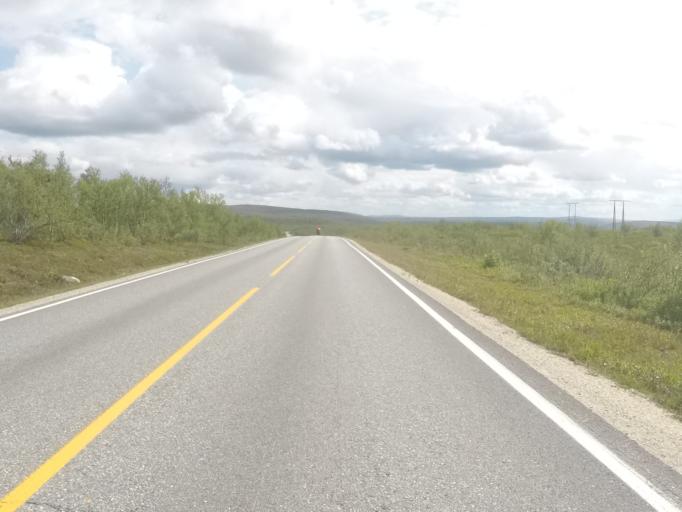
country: NO
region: Finnmark Fylke
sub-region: Karasjok
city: Karasjohka
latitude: 69.5551
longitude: 25.4021
